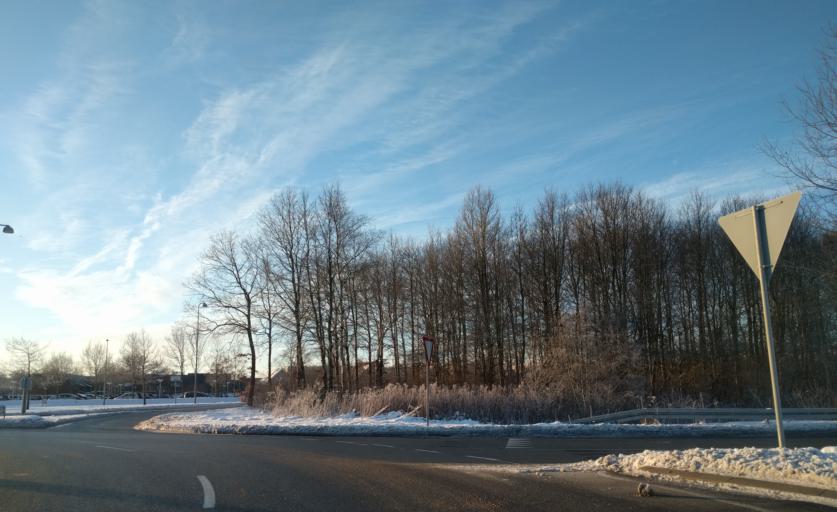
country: DK
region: North Denmark
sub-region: Alborg Kommune
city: Gistrup
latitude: 57.0196
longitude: 9.9754
